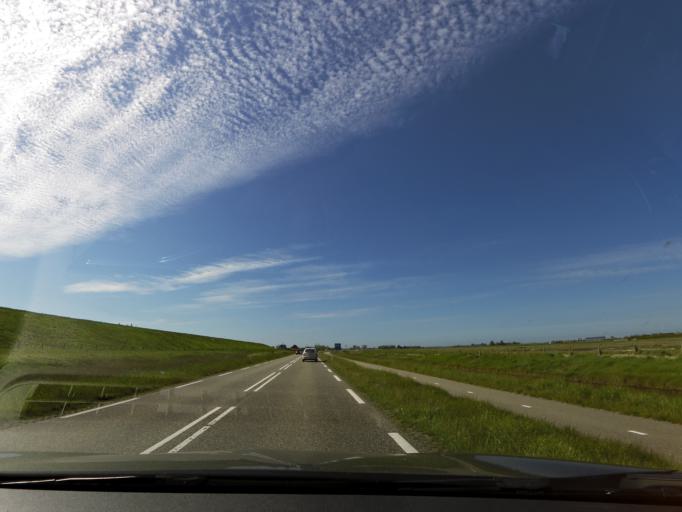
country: NL
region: Zeeland
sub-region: Schouwen-Duiveland
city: Scharendijke
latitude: 51.6717
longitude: 3.8717
